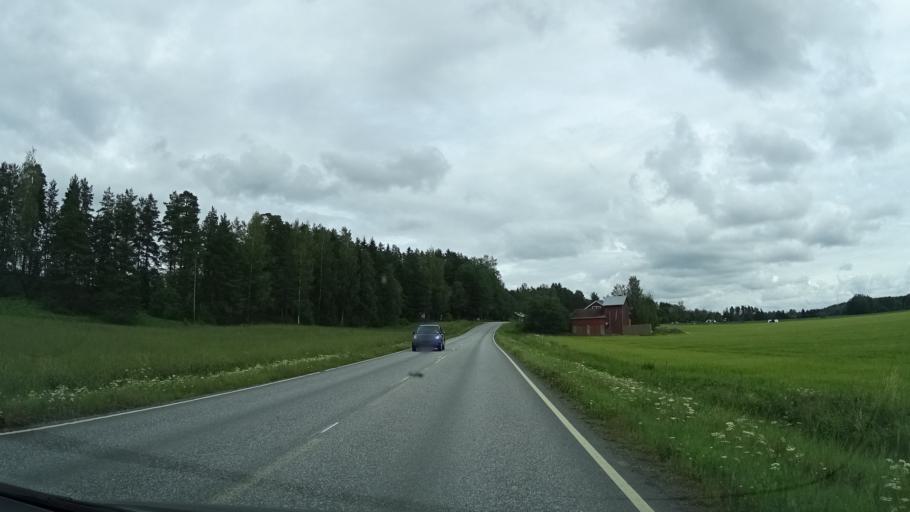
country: FI
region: Pirkanmaa
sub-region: Etelae-Pirkanmaa
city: Urjala
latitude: 61.0903
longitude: 23.4894
